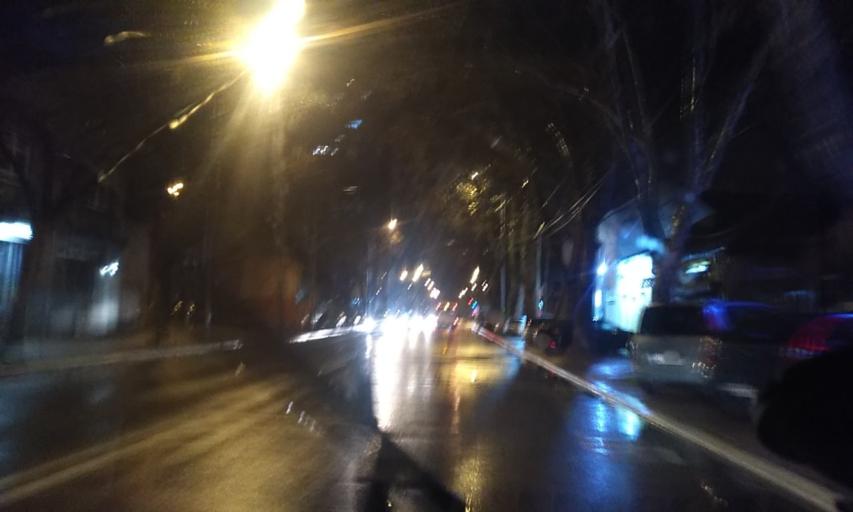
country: RS
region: Central Serbia
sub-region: Nisavski Okrug
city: Nis
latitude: 43.3219
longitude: 21.9014
